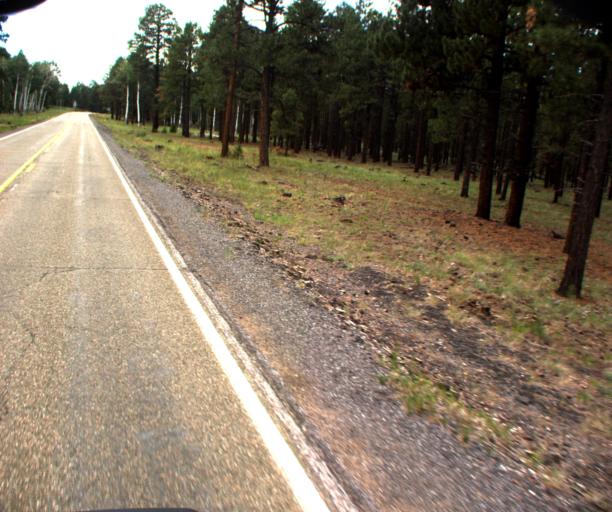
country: US
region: Arizona
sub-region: Coconino County
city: Parks
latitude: 35.3854
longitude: -111.7783
